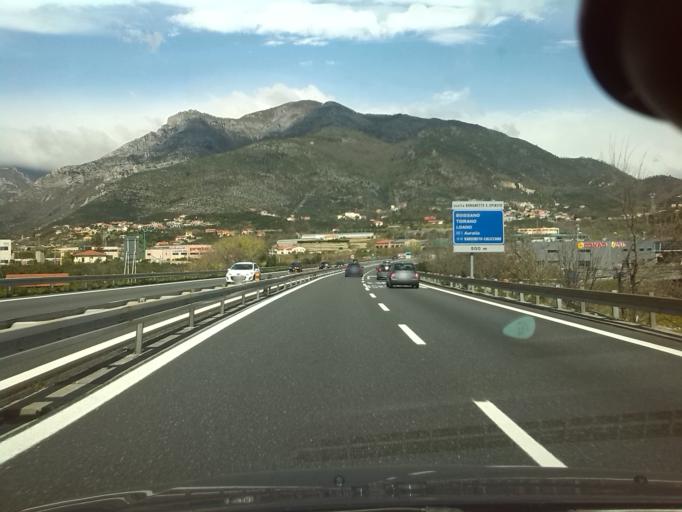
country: IT
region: Liguria
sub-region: Provincia di Savona
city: Borghetto Santo Spirito
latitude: 44.1179
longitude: 8.2263
